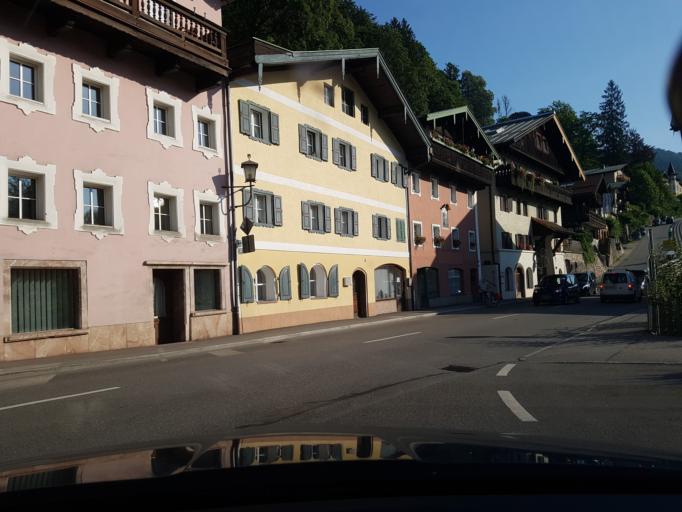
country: DE
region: Bavaria
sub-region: Upper Bavaria
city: Berchtesgaden
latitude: 47.6364
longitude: 13.0057
